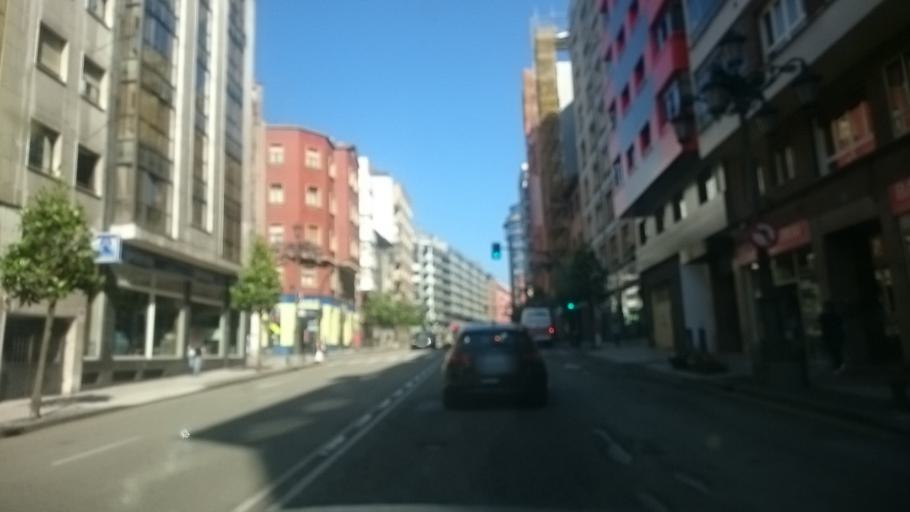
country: ES
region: Asturias
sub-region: Province of Asturias
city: Oviedo
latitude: 43.3561
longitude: -5.8525
